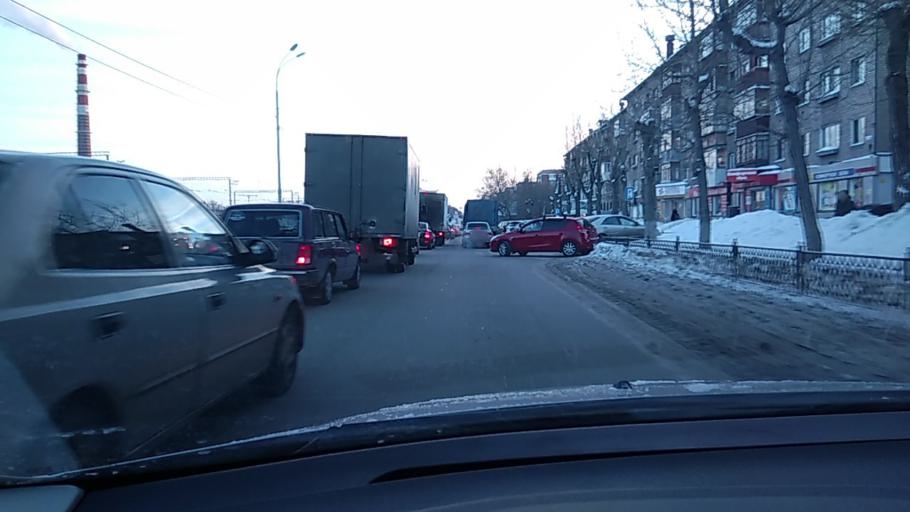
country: RU
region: Sverdlovsk
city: Yekaterinburg
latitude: 56.8402
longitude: 60.6324
